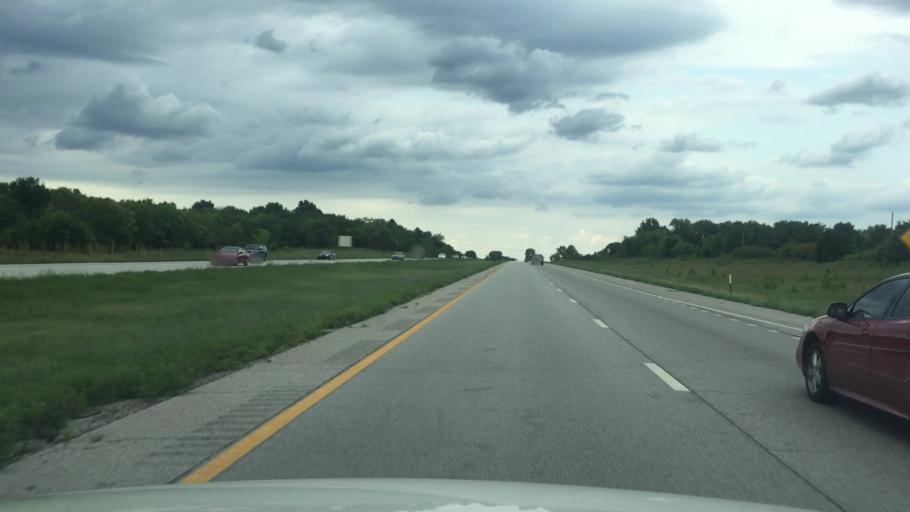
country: US
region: Kansas
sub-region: Johnson County
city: Spring Hill
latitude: 38.7712
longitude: -94.6777
